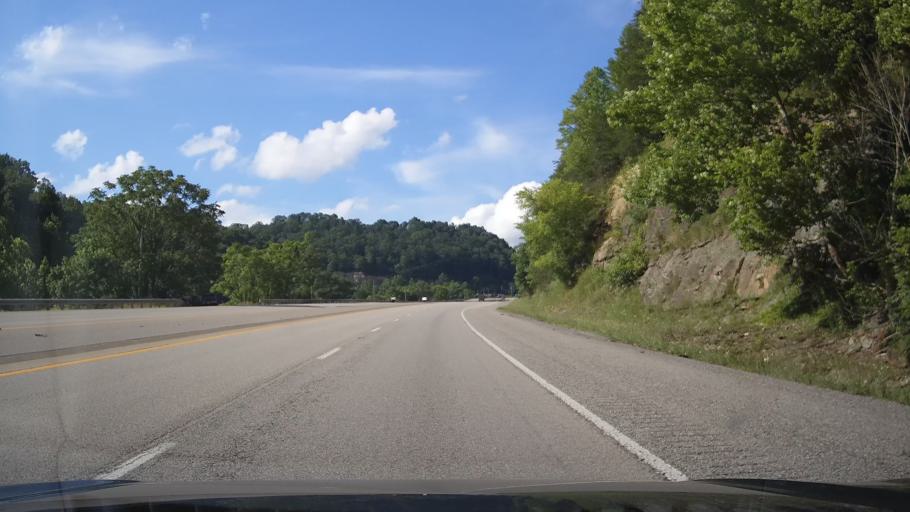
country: US
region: Kentucky
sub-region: Lawrence County
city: Louisa
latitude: 38.0281
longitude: -82.6525
